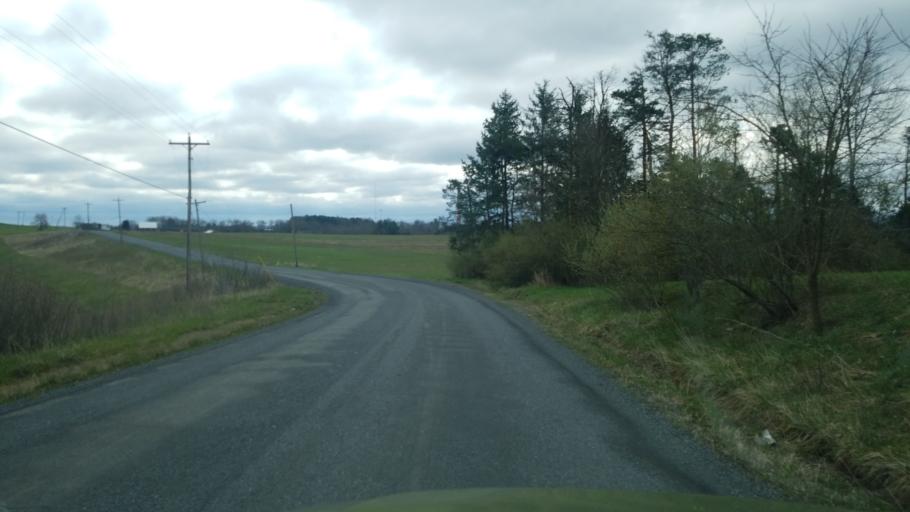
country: US
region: Pennsylvania
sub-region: Clearfield County
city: Clearfield
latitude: 41.0790
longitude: -78.3832
